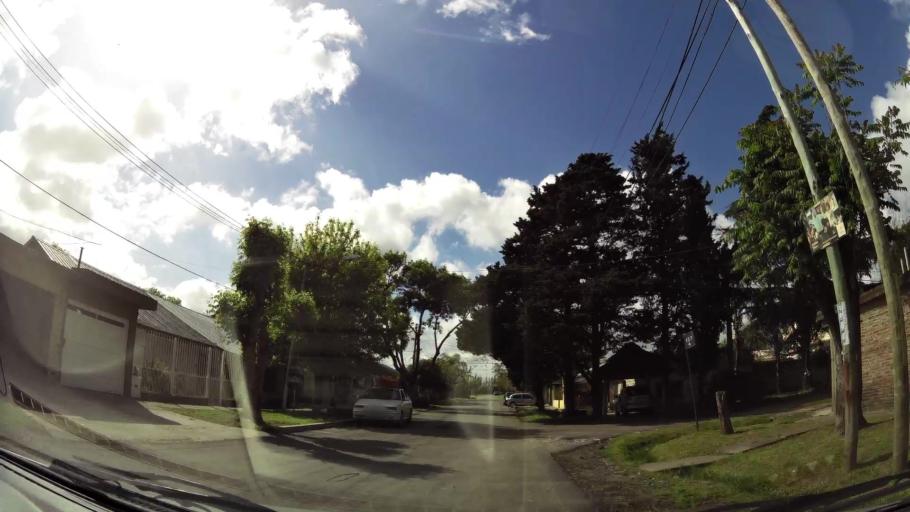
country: AR
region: Buenos Aires
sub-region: Partido de Quilmes
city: Quilmes
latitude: -34.7948
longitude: -58.1552
